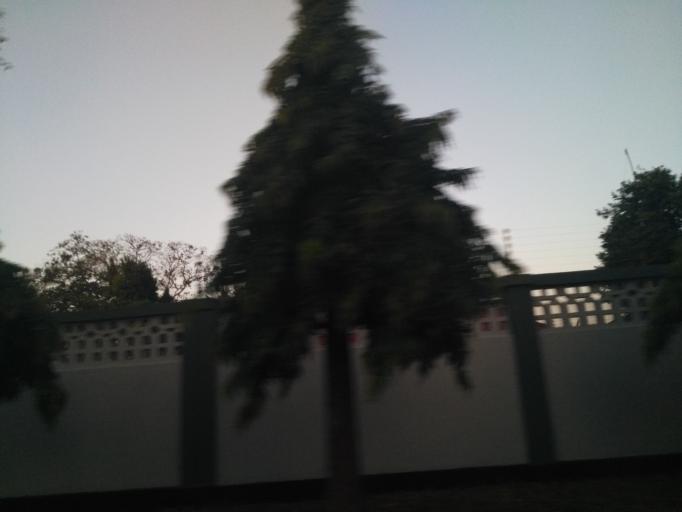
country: TZ
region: Dar es Salaam
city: Magomeni
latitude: -6.7669
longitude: 39.2779
